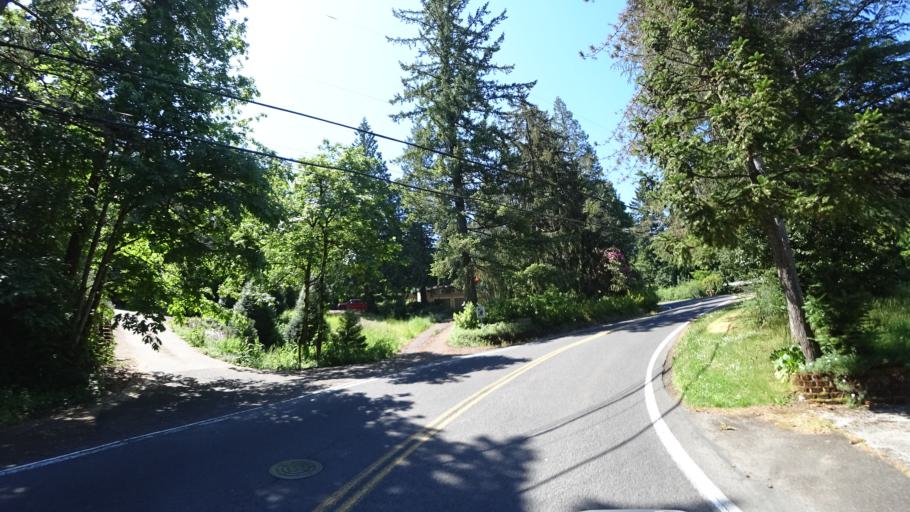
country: US
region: Oregon
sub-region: Clackamas County
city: Happy Valley
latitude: 45.4680
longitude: -122.5242
